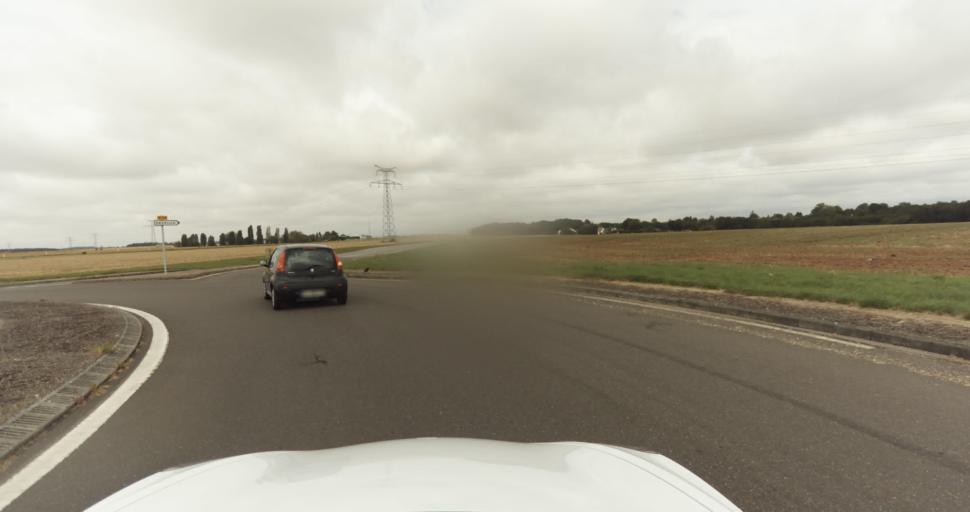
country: FR
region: Haute-Normandie
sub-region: Departement de l'Eure
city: Aviron
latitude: 49.0403
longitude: 1.0893
